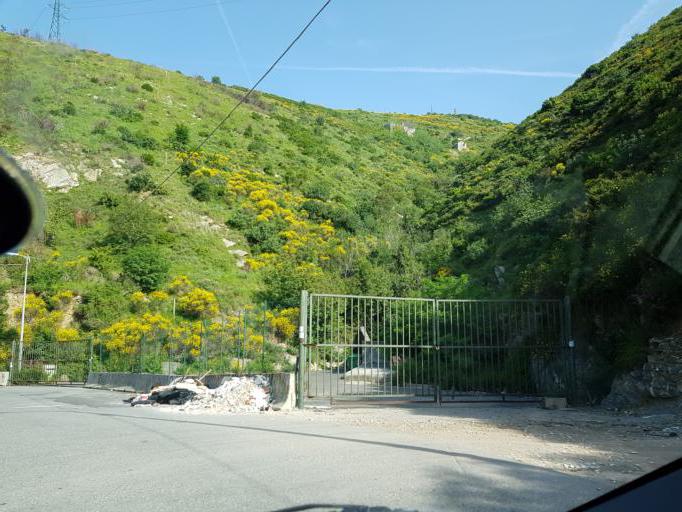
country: IT
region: Liguria
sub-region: Provincia di Genova
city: Genoa
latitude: 44.4291
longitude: 8.9195
